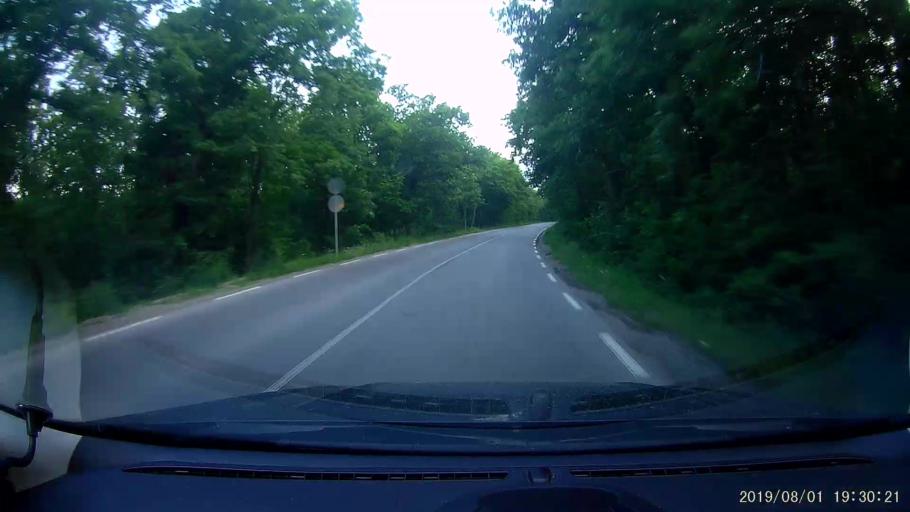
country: BG
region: Burgas
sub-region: Obshtina Sungurlare
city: Sungurlare
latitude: 42.8151
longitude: 26.8940
